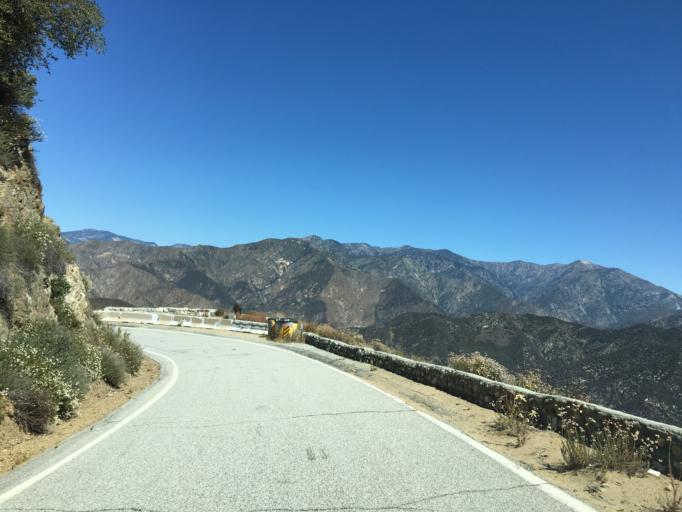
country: US
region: California
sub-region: San Bernardino County
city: San Antonio Heights
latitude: 34.2263
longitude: -117.7342
